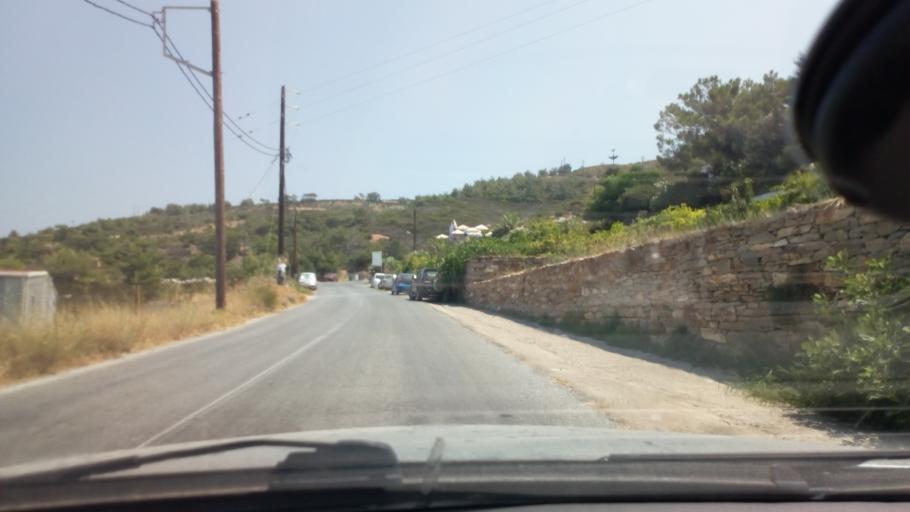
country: GR
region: North Aegean
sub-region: Nomos Samou
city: Agios Kirykos
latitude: 37.6333
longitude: 26.1250
